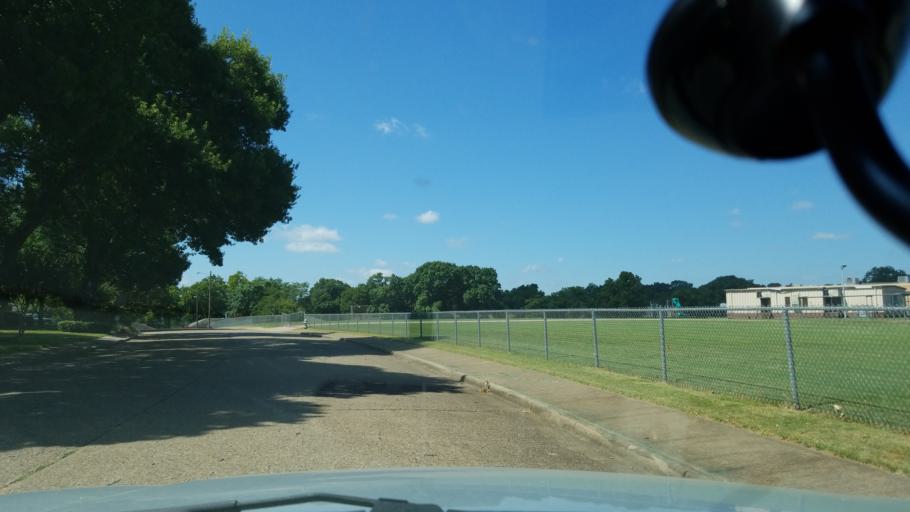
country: US
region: Texas
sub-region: Dallas County
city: Cockrell Hill
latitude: 32.6846
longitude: -96.8323
